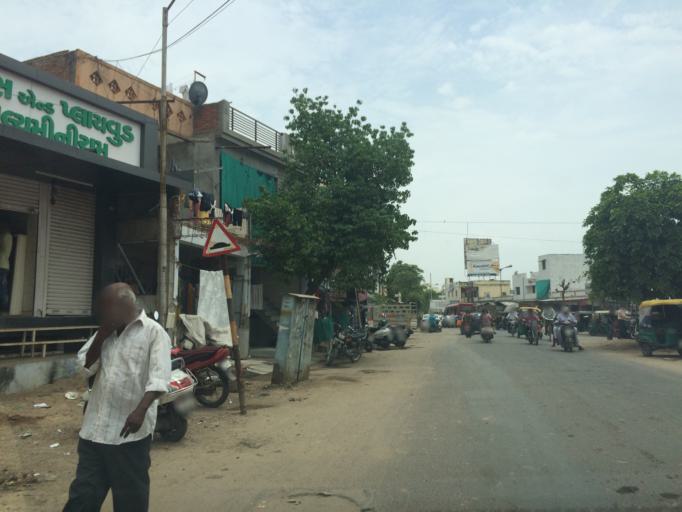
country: IN
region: Gujarat
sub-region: Ahmadabad
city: Ahmedabad
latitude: 23.0859
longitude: 72.5648
